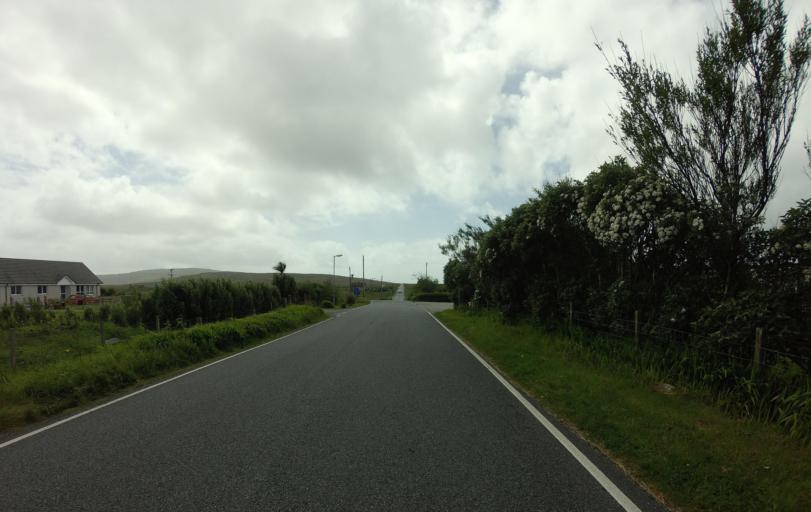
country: GB
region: Scotland
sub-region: Eilean Siar
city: Isle of South Uist
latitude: 57.1585
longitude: -7.3701
